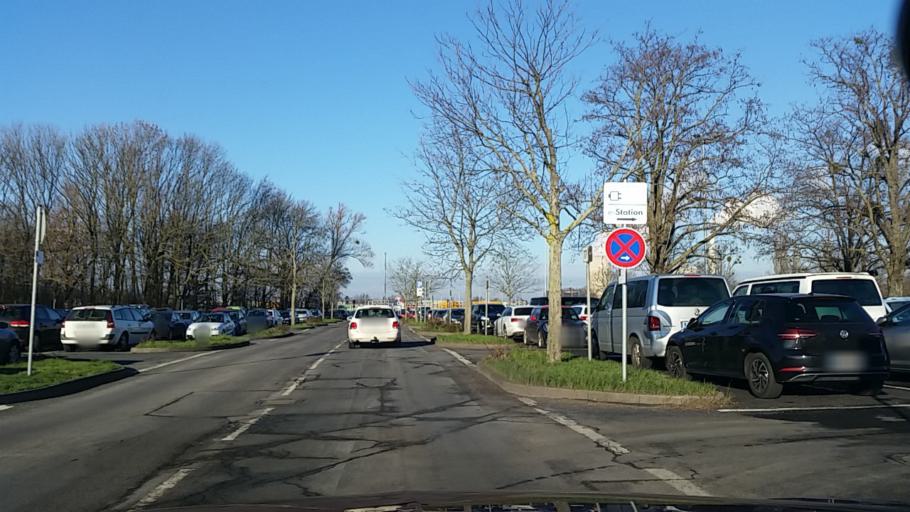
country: DE
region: Lower Saxony
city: Wolfsburg
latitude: 52.4306
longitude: 10.7596
